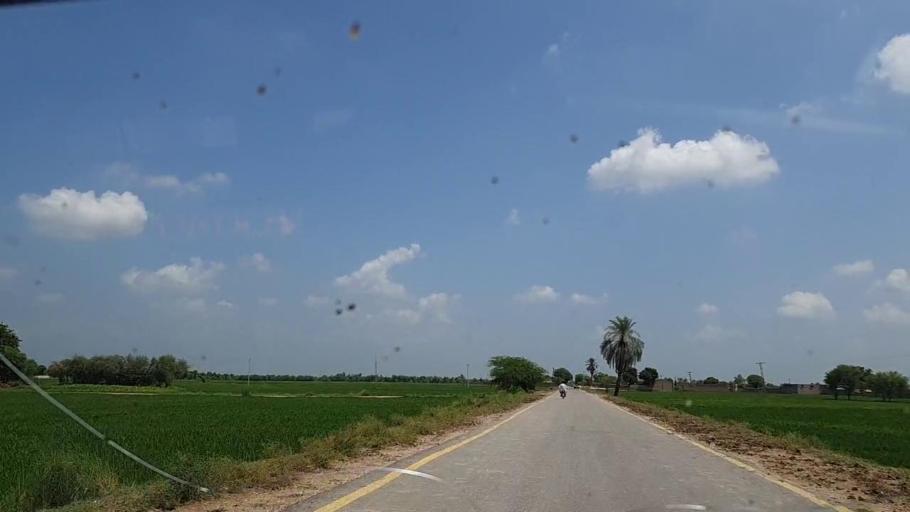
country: PK
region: Sindh
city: Tharu Shah
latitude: 26.9815
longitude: 68.0820
